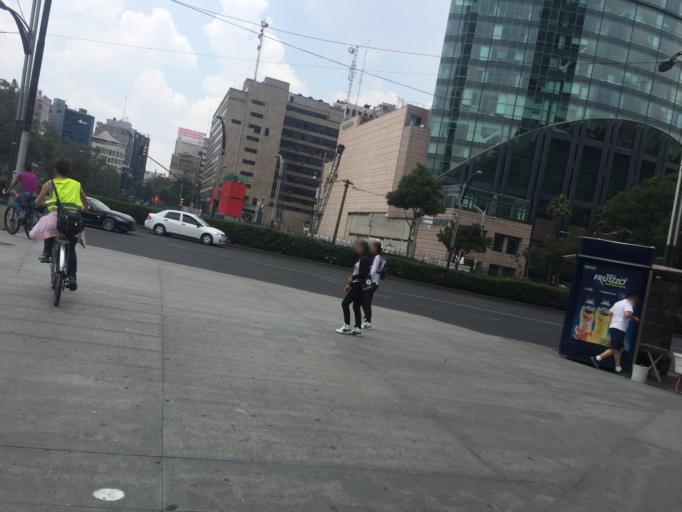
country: MX
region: Mexico City
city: Polanco
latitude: 19.4232
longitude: -99.1755
